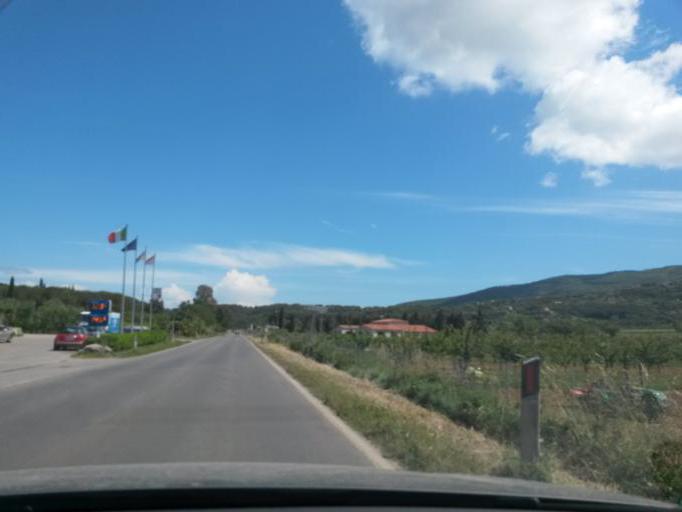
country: IT
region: Tuscany
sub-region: Provincia di Livorno
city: Capoliveri
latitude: 42.7601
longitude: 10.3699
